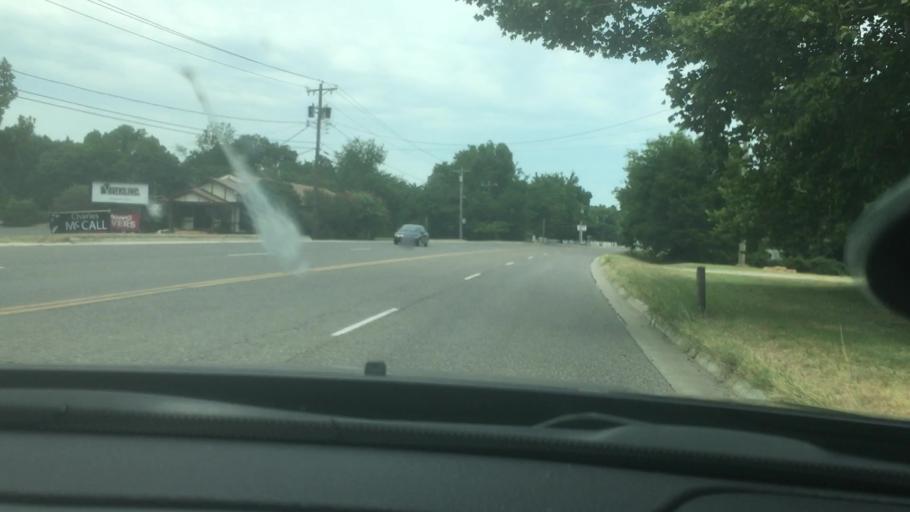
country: US
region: Oklahoma
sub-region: Murray County
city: Davis
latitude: 34.4738
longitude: -97.1317
